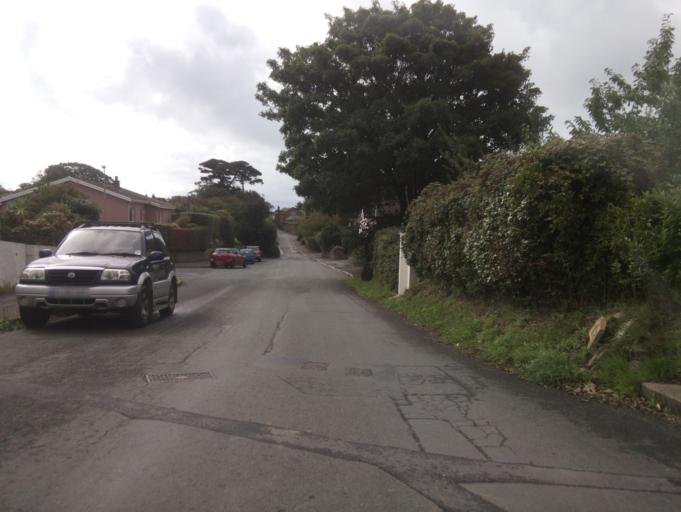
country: GB
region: England
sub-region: Devon
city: Dartmouth
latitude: 50.3279
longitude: -3.6004
